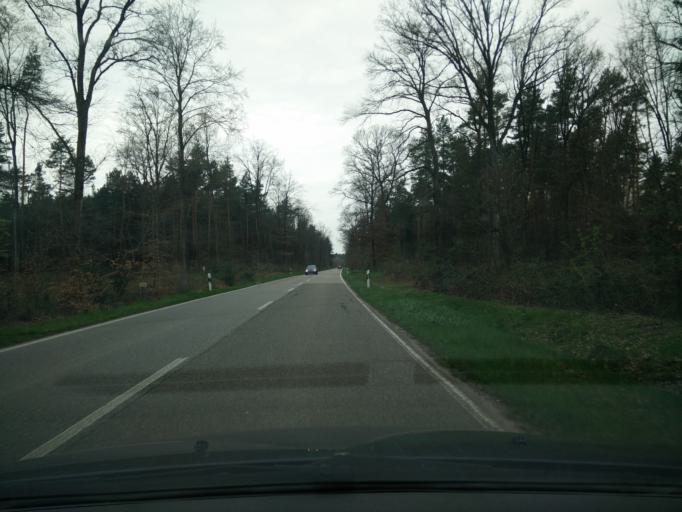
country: DE
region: Rheinland-Pfalz
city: Freckenfeld
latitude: 49.0464
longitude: 8.0972
